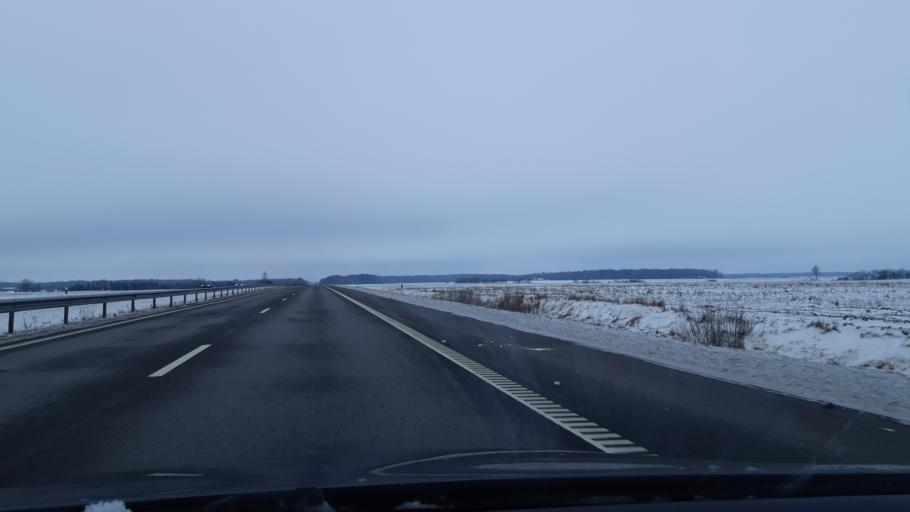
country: LT
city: Vilkija
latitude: 55.1141
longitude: 23.7677
